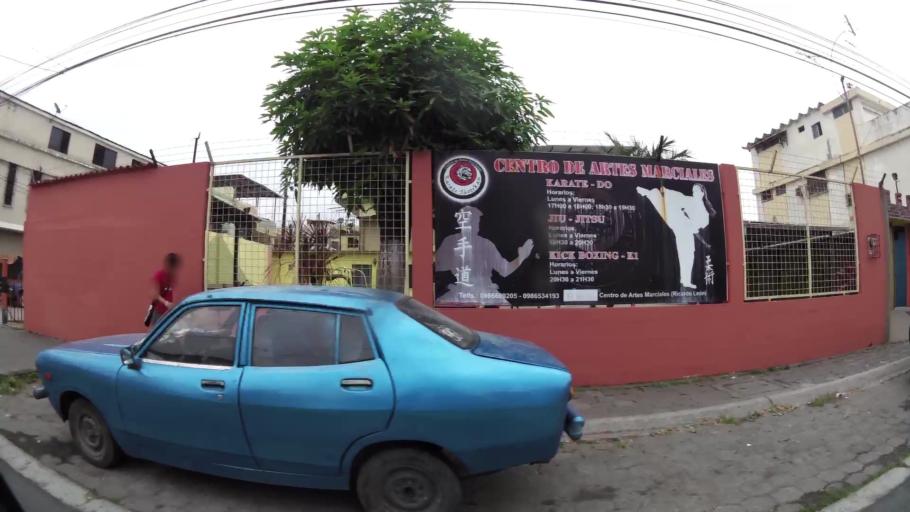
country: EC
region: Guayas
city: Eloy Alfaro
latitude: -2.1400
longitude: -79.9059
